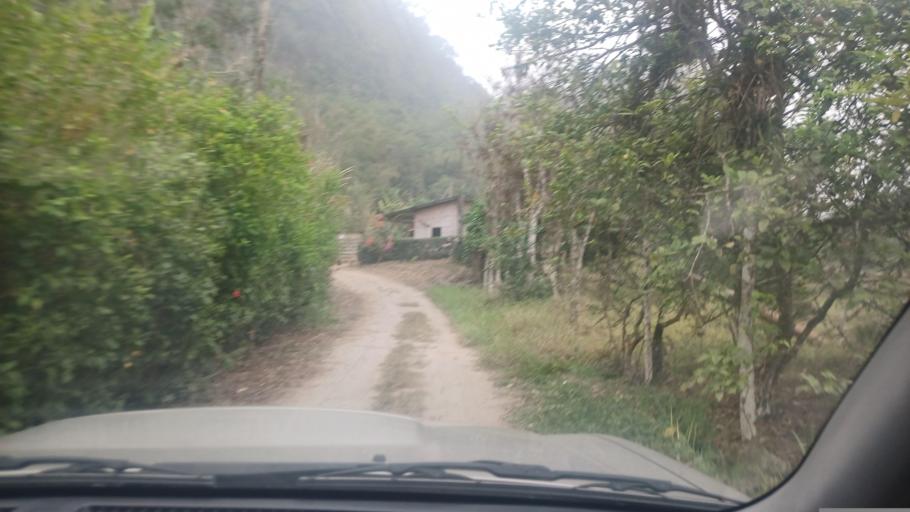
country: EC
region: Santo Domingo de los Tsachilas
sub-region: Canton Santo Domingo de los Colorados
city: Santo Domingo de los Colorados
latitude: -0.2798
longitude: -79.0689
